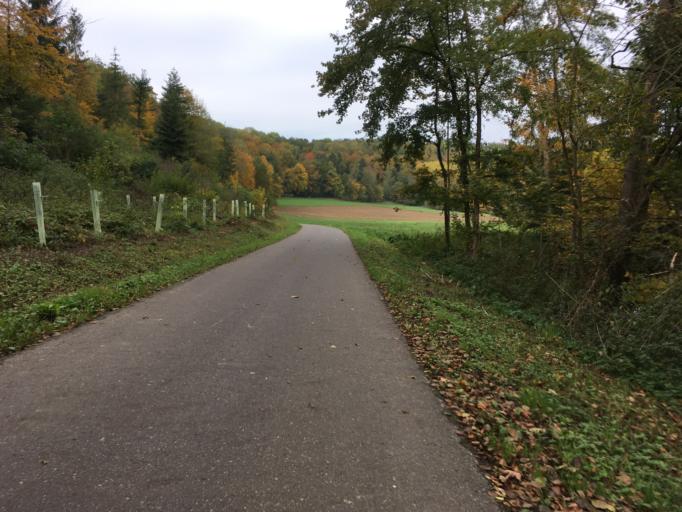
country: DE
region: Baden-Wuerttemberg
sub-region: Karlsruhe Region
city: Adelsheim
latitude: 49.3864
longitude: 9.3894
